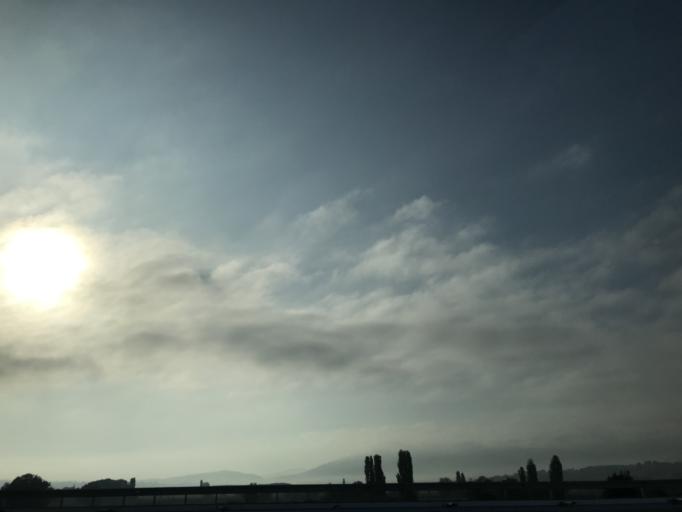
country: TR
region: Balikesir
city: Gobel
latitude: 39.9936
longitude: 28.1901
